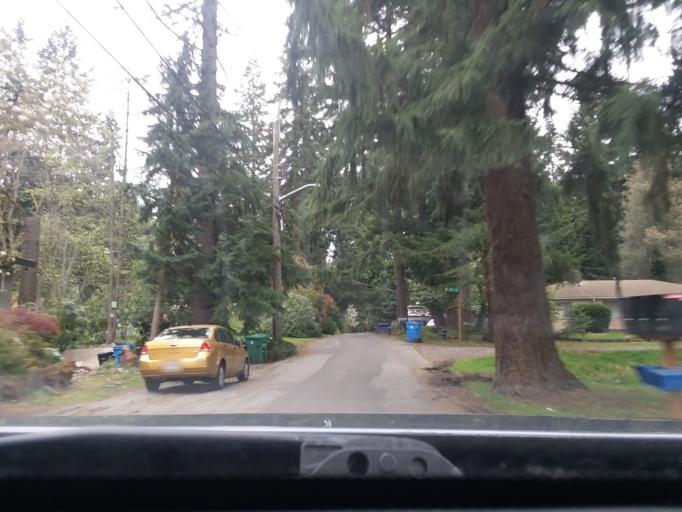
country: US
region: Washington
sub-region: King County
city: Shoreline
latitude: 47.7366
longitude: -122.3480
